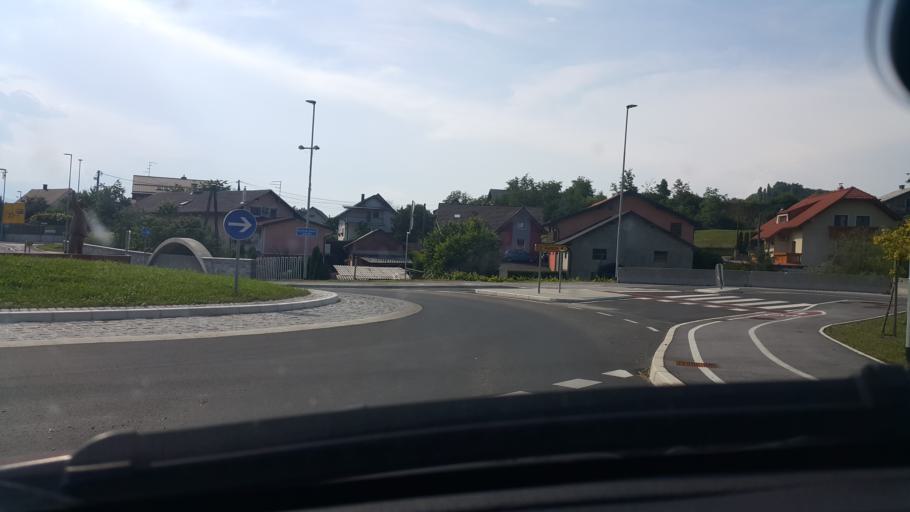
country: SI
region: Duplek
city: Spodnji Duplek
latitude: 46.5007
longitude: 15.7563
